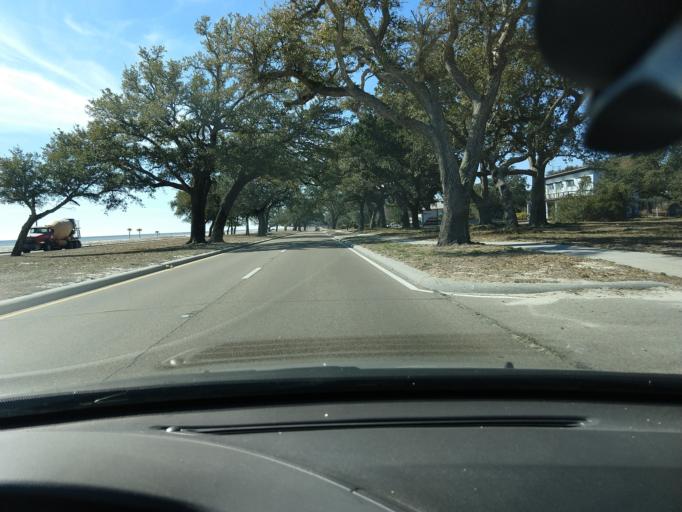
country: US
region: Mississippi
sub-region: Harrison County
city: Long Beach
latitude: 30.3423
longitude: -89.1583
